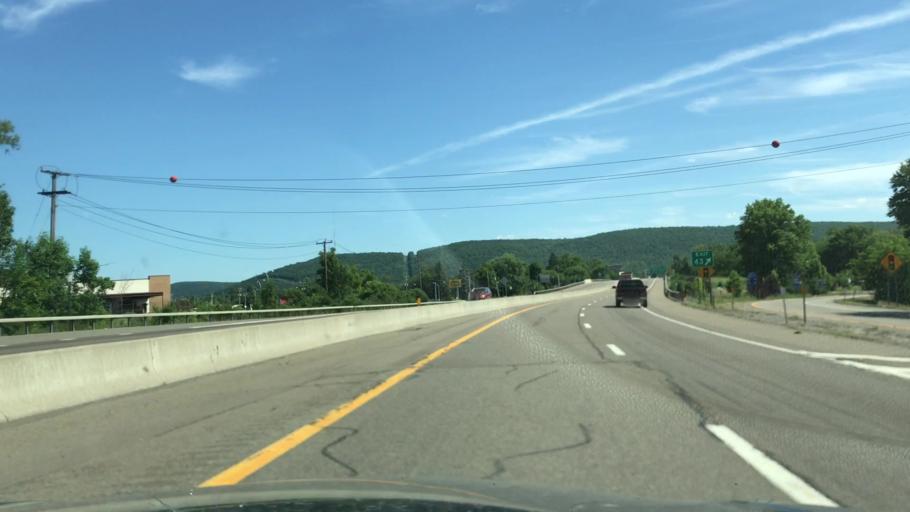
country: US
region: New York
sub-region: Steuben County
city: Painted Post
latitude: 42.1731
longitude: -77.1056
